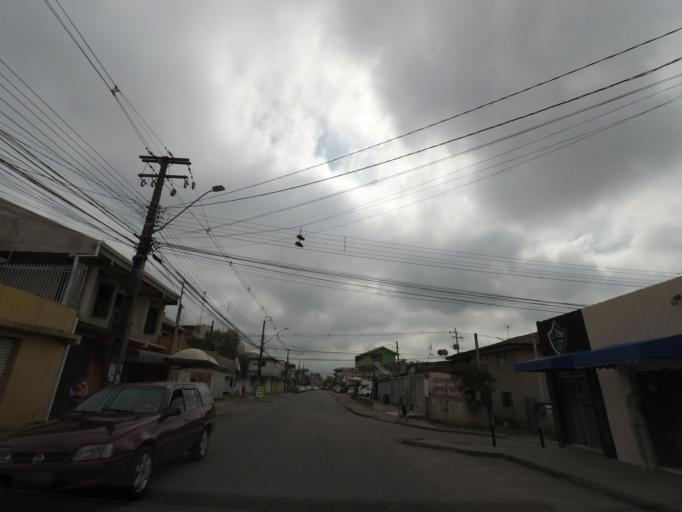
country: BR
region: Parana
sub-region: Curitiba
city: Curitiba
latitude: -25.4981
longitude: -49.3379
